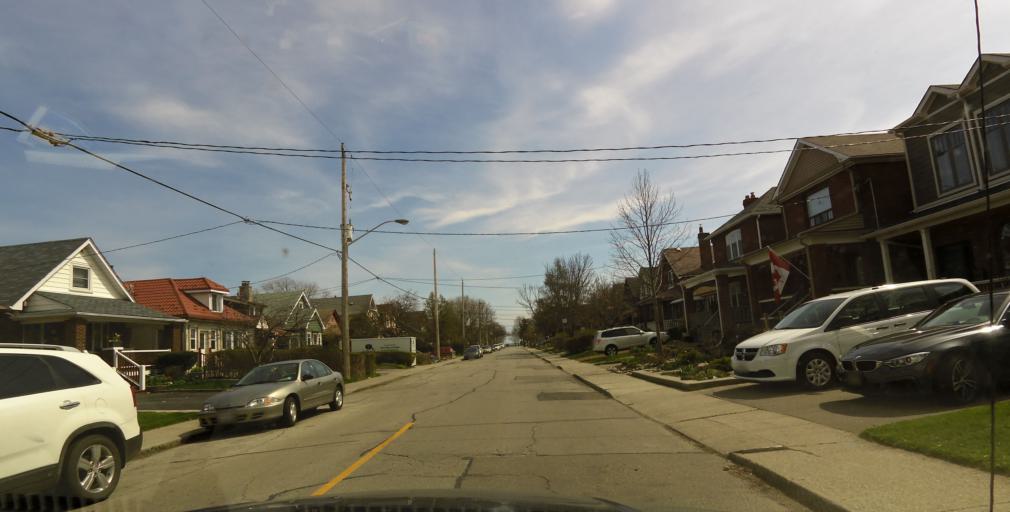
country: CA
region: Ontario
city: Etobicoke
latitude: 43.5986
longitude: -79.5031
